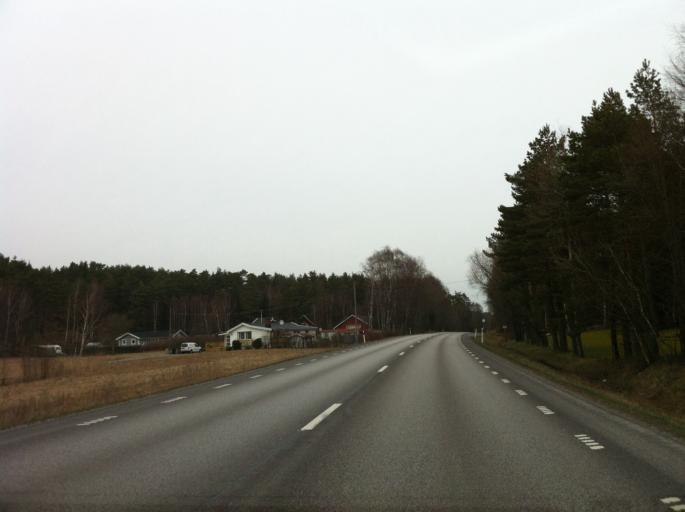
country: SE
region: Vaestra Goetaland
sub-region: Tjorns Kommun
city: Myggenas
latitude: 58.0017
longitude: 11.6668
